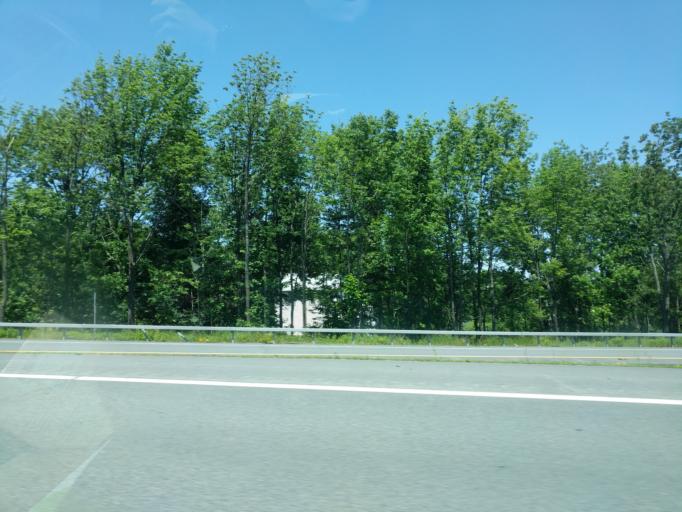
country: US
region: New York
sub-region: Sullivan County
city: Monticello
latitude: 41.6643
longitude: -74.6805
